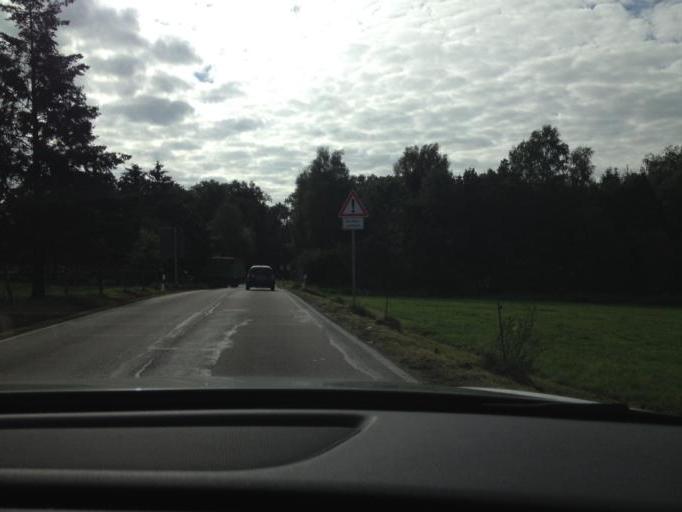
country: DE
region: Saarland
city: Mainzweiler
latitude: 49.4007
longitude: 7.1077
